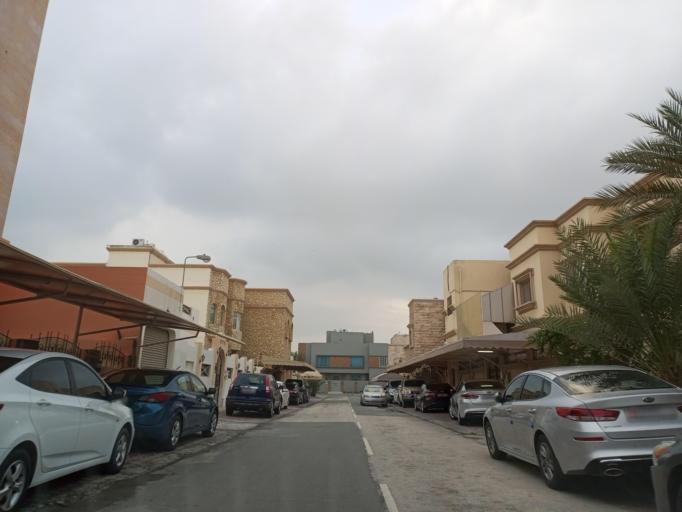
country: BH
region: Muharraq
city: Al Hadd
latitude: 26.2421
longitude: 50.6494
